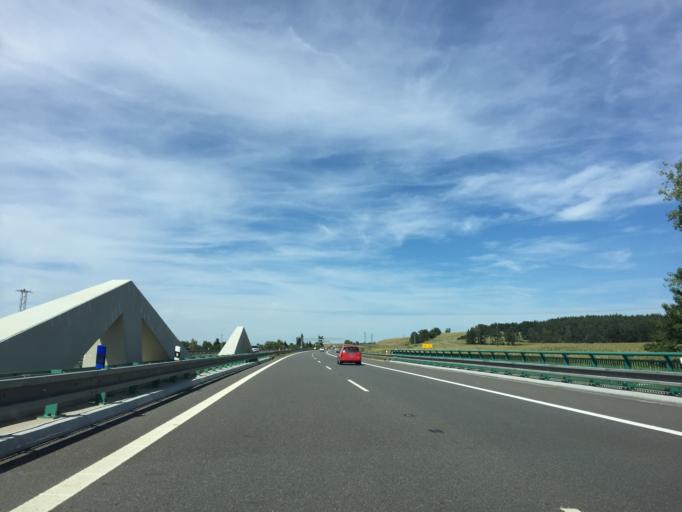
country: CZ
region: Jihocesky
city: Sobeslav
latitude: 49.2431
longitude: 14.7286
